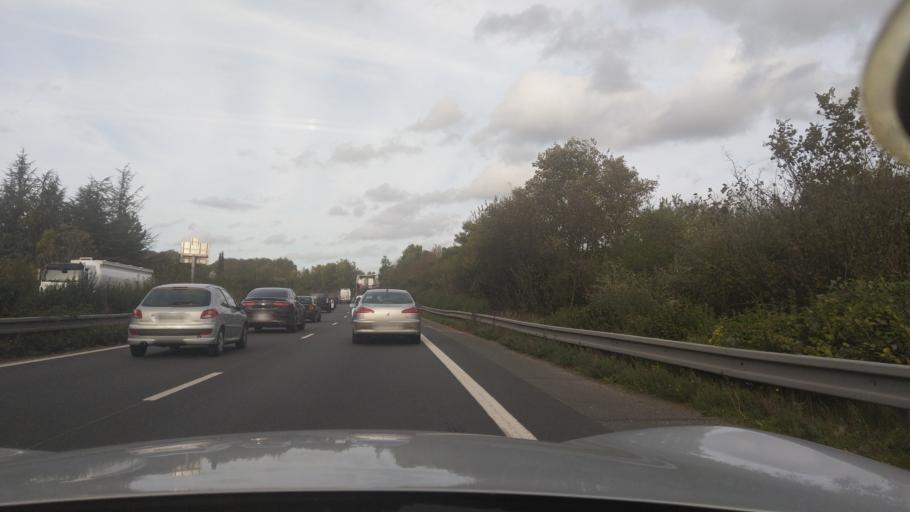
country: FR
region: Ile-de-France
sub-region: Departement du Val-d'Oise
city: Frepillon
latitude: 49.0582
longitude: 2.2094
